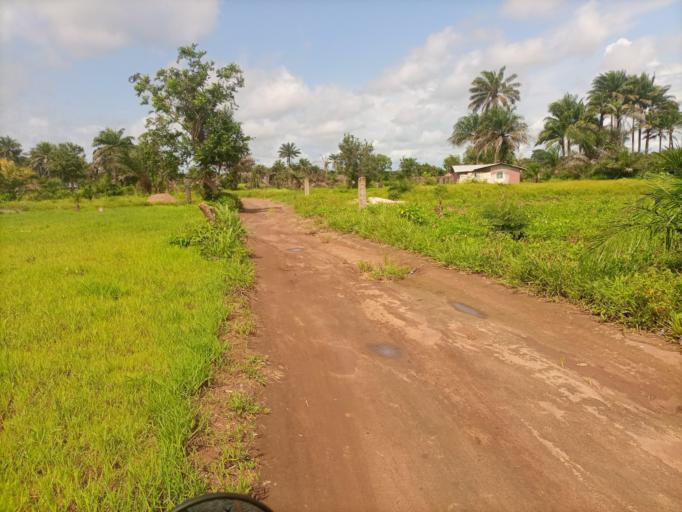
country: SL
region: Northern Province
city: Sawkta
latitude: 8.6386
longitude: -13.2093
